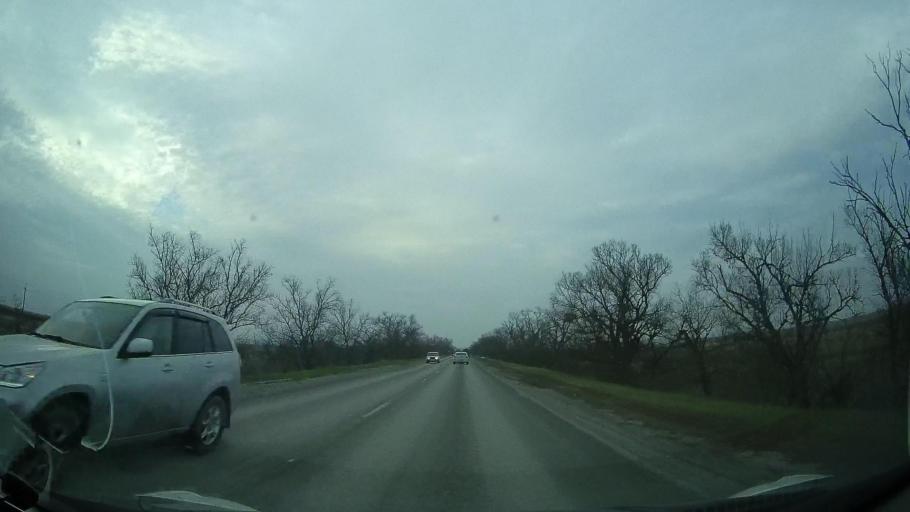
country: RU
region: Rostov
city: Ol'ginskaya
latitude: 47.2077
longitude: 39.9228
